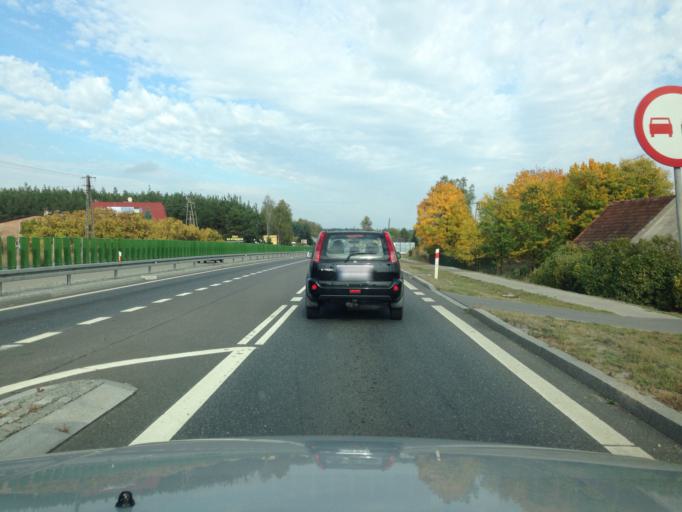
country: PL
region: Kujawsko-Pomorskie
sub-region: Grudziadz
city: Grudziadz
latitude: 53.5030
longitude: 18.6827
